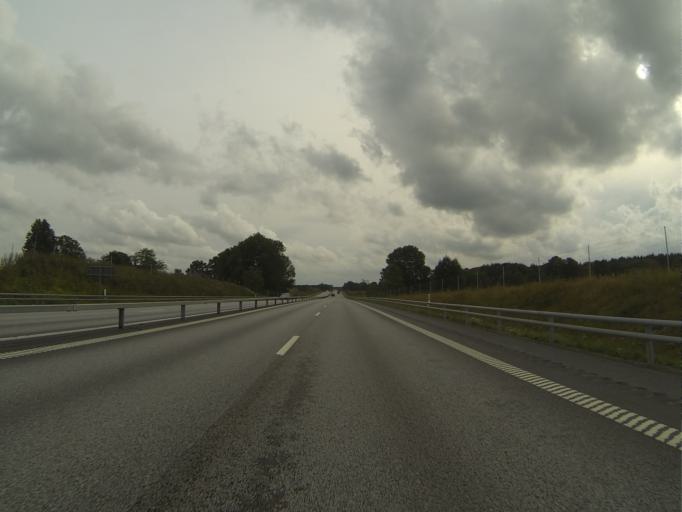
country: SE
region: Skane
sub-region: Horby Kommun
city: Hoerby
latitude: 55.8908
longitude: 13.7198
